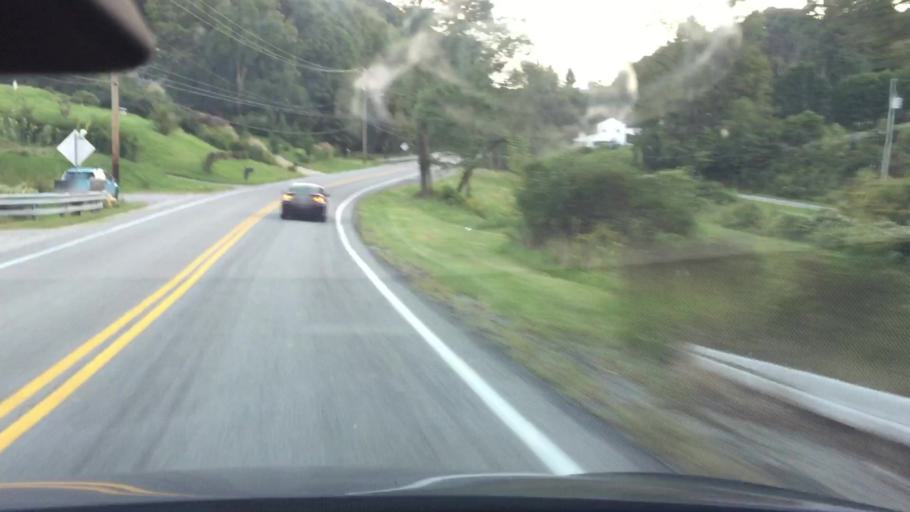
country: US
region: Pennsylvania
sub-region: Allegheny County
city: Allison Park
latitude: 40.5402
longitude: -79.9194
